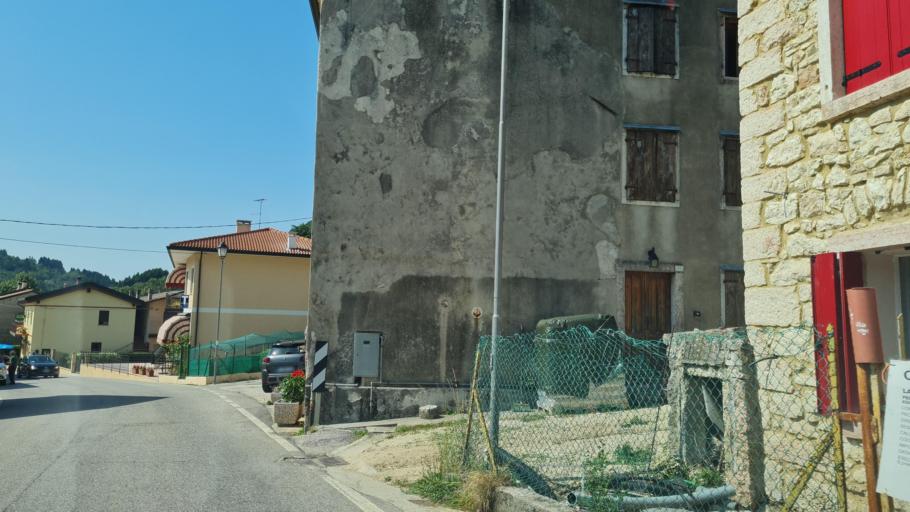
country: IT
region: Veneto
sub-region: Provincia di Vicenza
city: Conco
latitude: 45.7941
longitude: 11.6105
